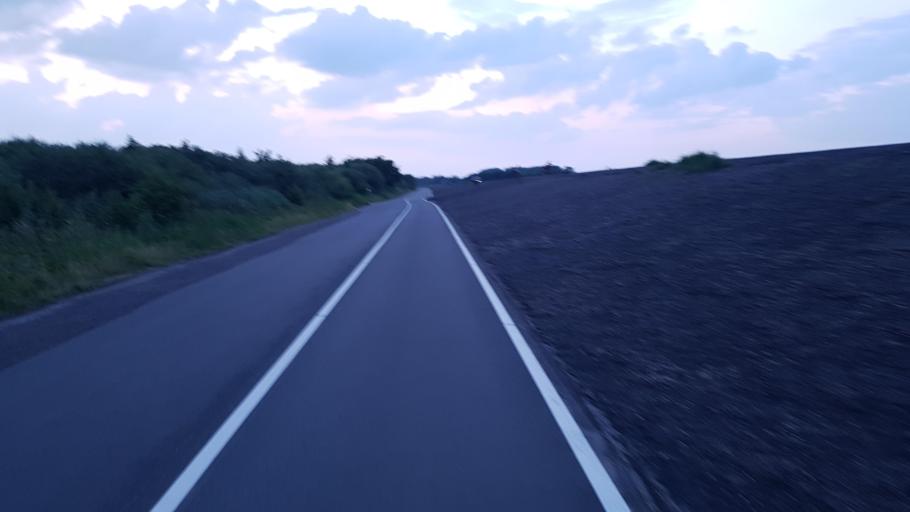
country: DE
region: Schleswig-Holstein
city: Sankt Peter-Ording
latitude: 54.2971
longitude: 8.6363
